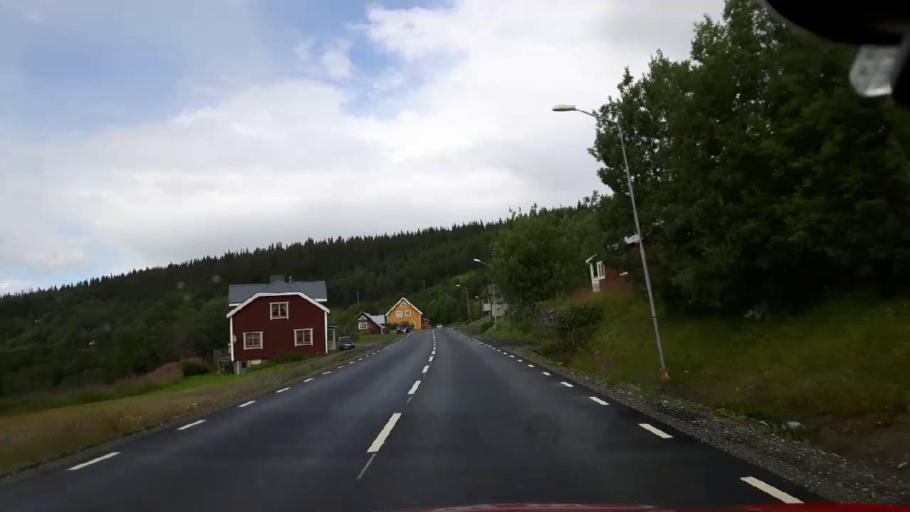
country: NO
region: Nord-Trondelag
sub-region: Royrvik
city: Royrvik
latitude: 64.8351
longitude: 14.1085
